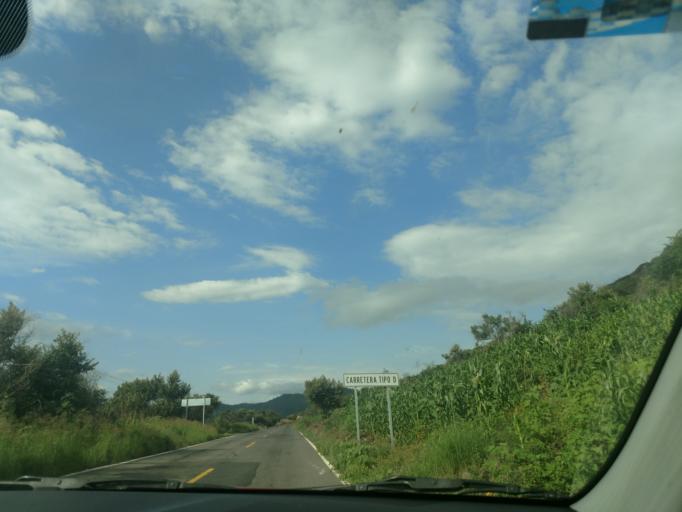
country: MX
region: Jalisco
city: Ameca
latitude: 20.5331
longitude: -104.2033
